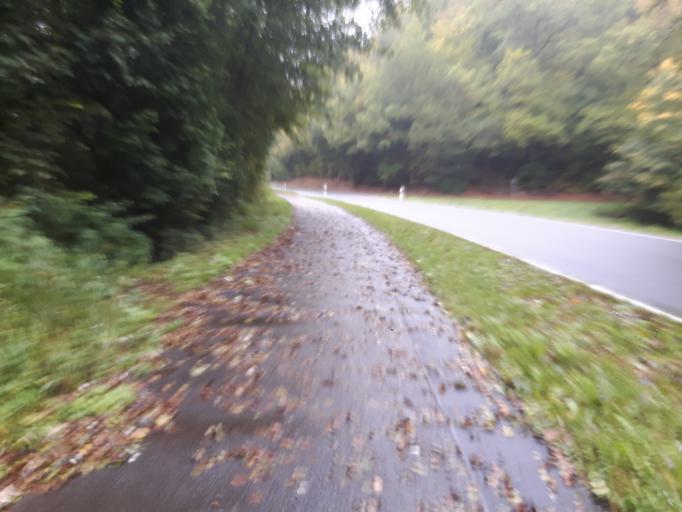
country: DE
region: Bavaria
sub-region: Regierungsbezirk Unterfranken
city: Neuendorf
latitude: 50.0293
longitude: 9.6530
